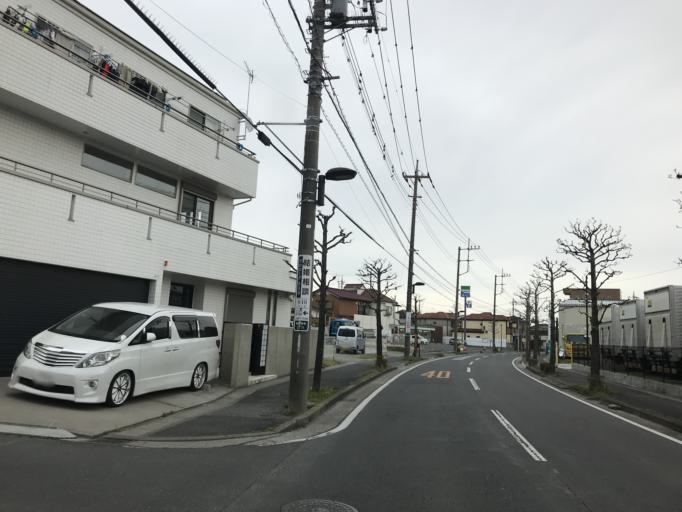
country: JP
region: Saitama
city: Yashio-shi
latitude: 35.8275
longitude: 139.8420
